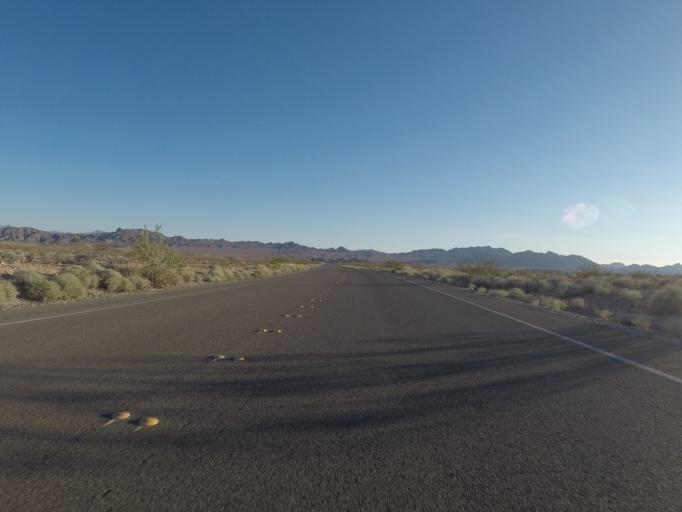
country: US
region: Nevada
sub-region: Clark County
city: Moapa Valley
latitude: 36.3210
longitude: -114.4929
